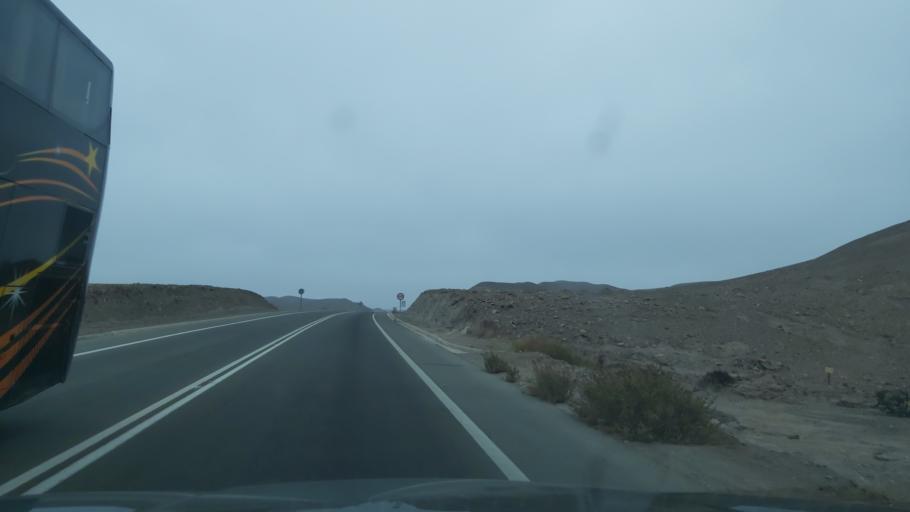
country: CL
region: Atacama
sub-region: Provincia de Copiapo
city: Copiapo
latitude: -27.2894
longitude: -70.1418
